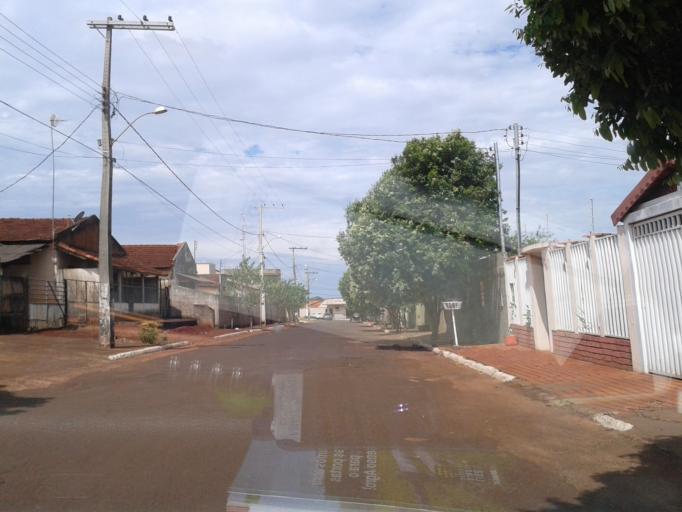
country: BR
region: Goias
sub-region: Itumbiara
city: Itumbiara
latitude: -18.4324
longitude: -49.1896
